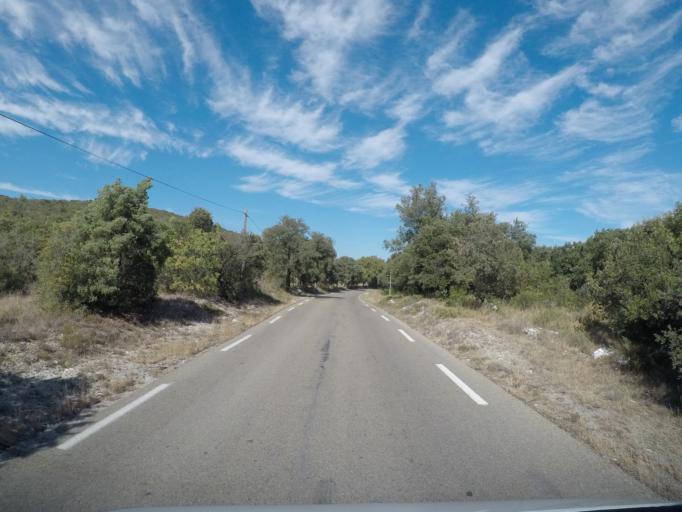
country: FR
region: Languedoc-Roussillon
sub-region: Departement du Gard
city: Anduze
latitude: 44.0032
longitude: 3.9802
